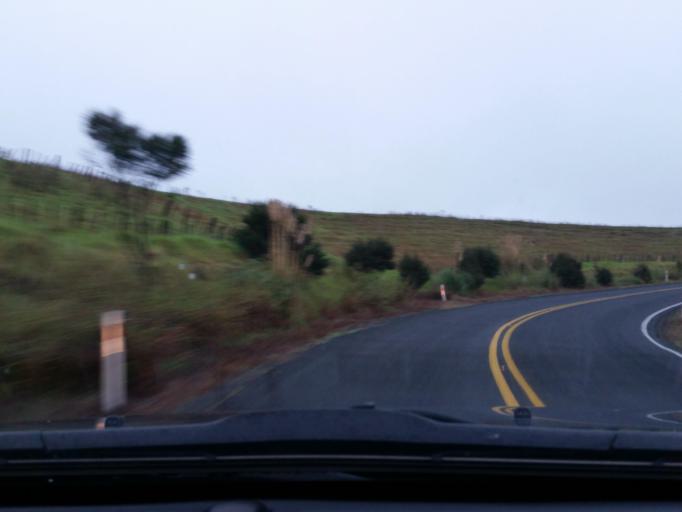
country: NZ
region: Northland
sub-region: Kaipara District
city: Dargaville
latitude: -35.8378
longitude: 174.0317
